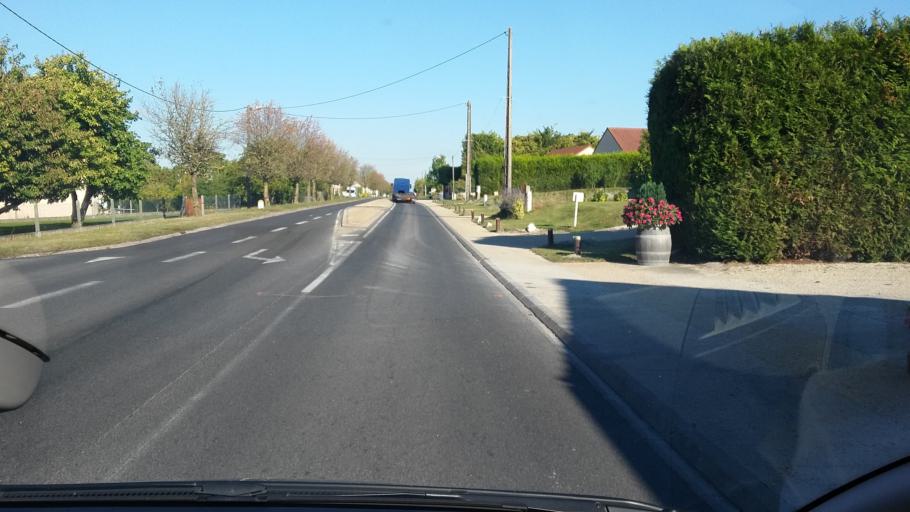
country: FR
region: Champagne-Ardenne
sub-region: Departement de la Marne
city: Vertus
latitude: 48.8760
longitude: 4.0000
